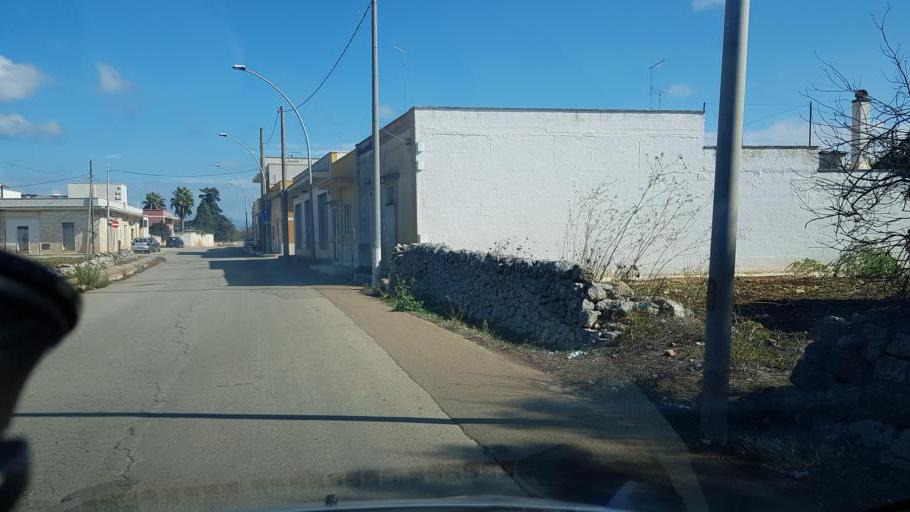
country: IT
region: Apulia
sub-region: Provincia di Brindisi
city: San Vito dei Normanni
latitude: 40.6599
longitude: 17.7135
